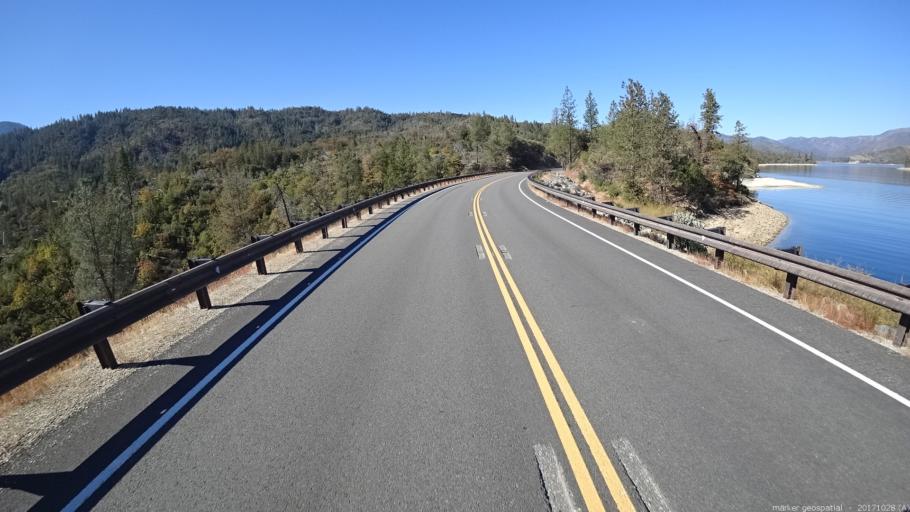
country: US
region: California
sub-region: Shasta County
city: Shasta
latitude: 40.5981
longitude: -122.5462
